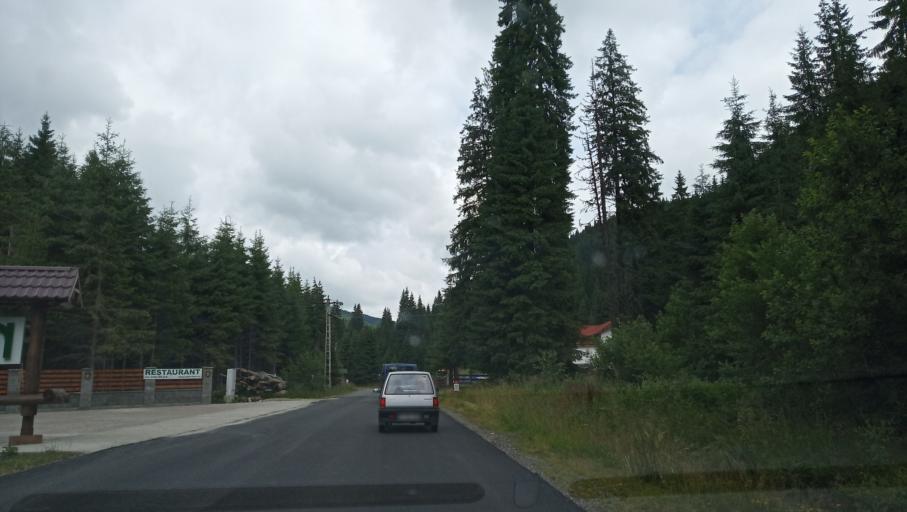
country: RO
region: Hunedoara
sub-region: Oras Petrila
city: Petrila
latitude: 45.4348
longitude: 23.6366
